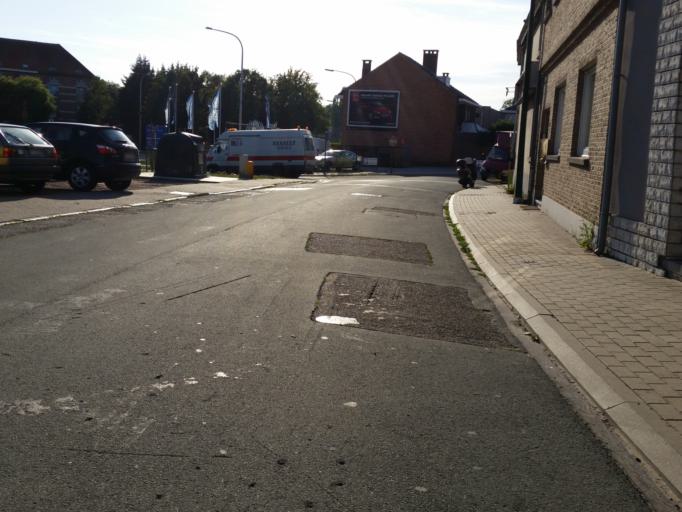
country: BE
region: Flanders
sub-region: Provincie Vlaams-Brabant
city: Diegem
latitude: 50.8963
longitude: 4.4358
